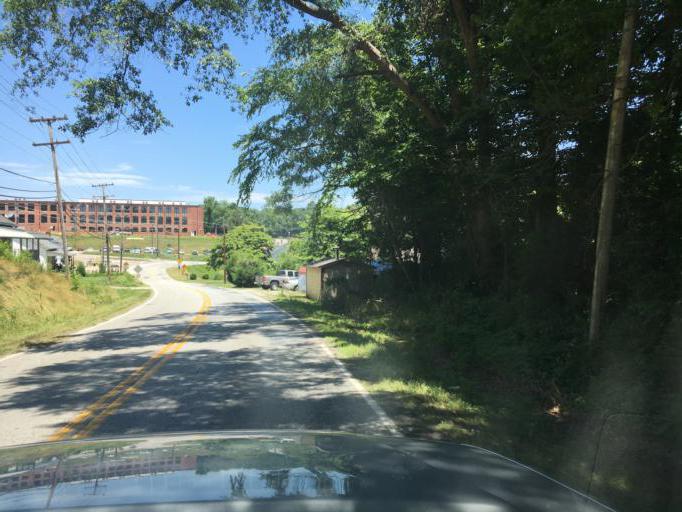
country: US
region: South Carolina
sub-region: Greenville County
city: Greer
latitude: 34.9597
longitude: -82.2080
